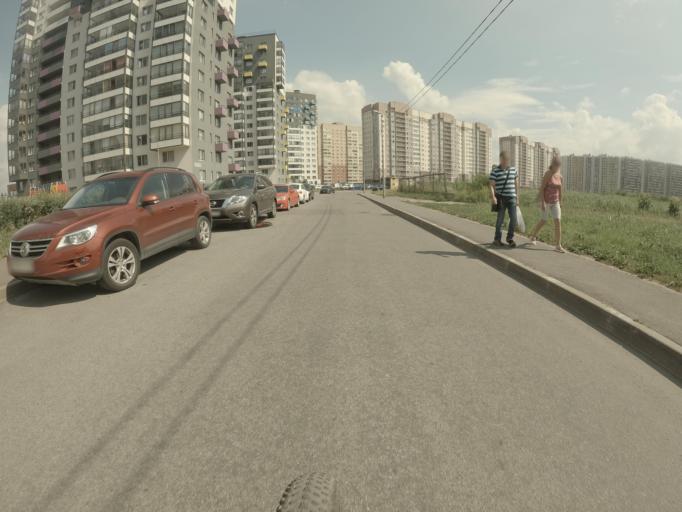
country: RU
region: St.-Petersburg
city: Krasnogvargeisky
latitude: 59.9199
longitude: 30.4363
